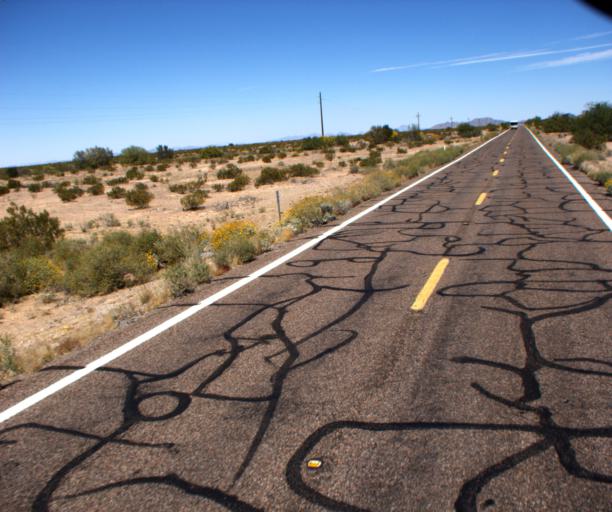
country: US
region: Arizona
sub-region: Pima County
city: Ajo
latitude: 32.6340
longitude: -112.8643
